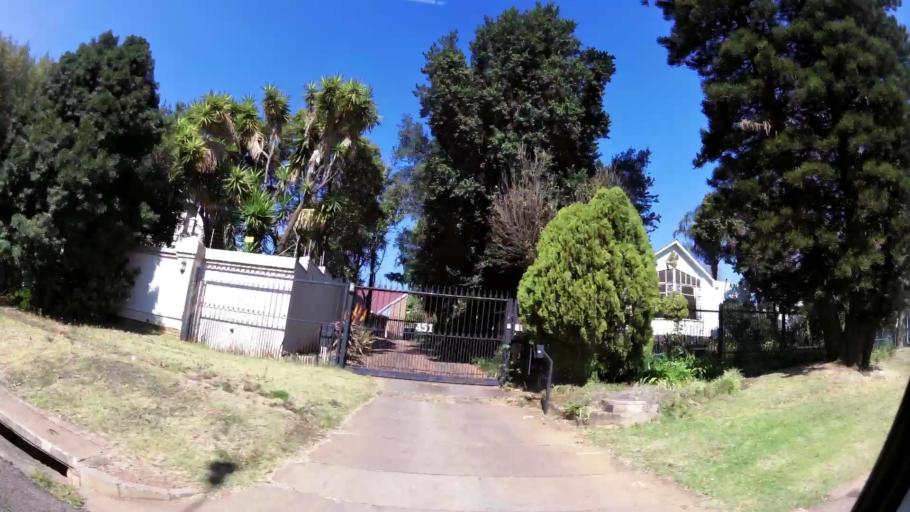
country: ZA
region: Gauteng
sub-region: City of Tshwane Metropolitan Municipality
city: Pretoria
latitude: -25.7571
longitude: 28.2672
